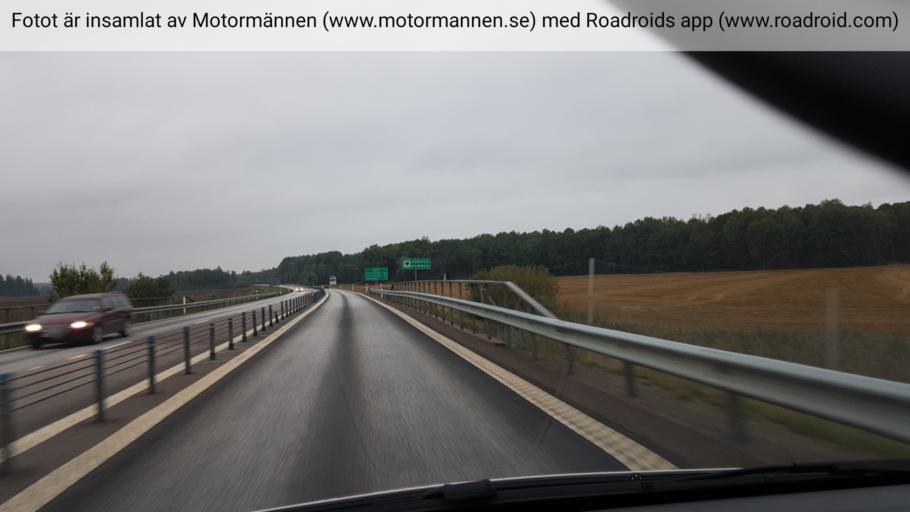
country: SE
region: Vaestmanland
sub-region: Arboga Kommun
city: Arboga
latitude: 59.4242
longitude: 15.8886
